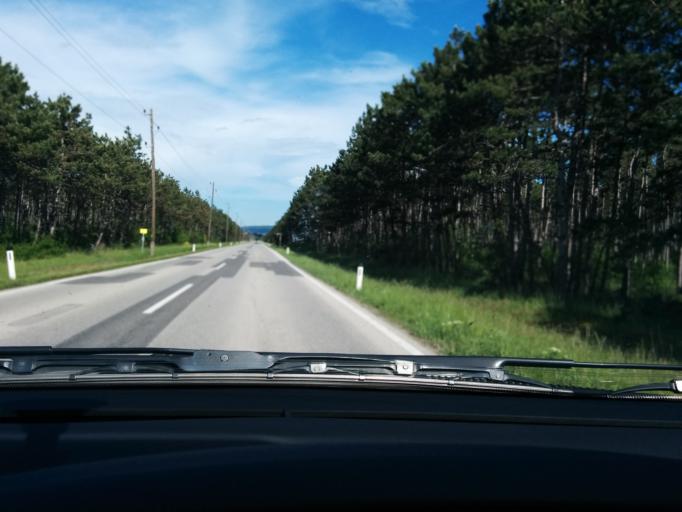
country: AT
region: Lower Austria
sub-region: Politischer Bezirk Wiener Neustadt
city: Zillingdorf
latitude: 47.8912
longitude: 16.3146
